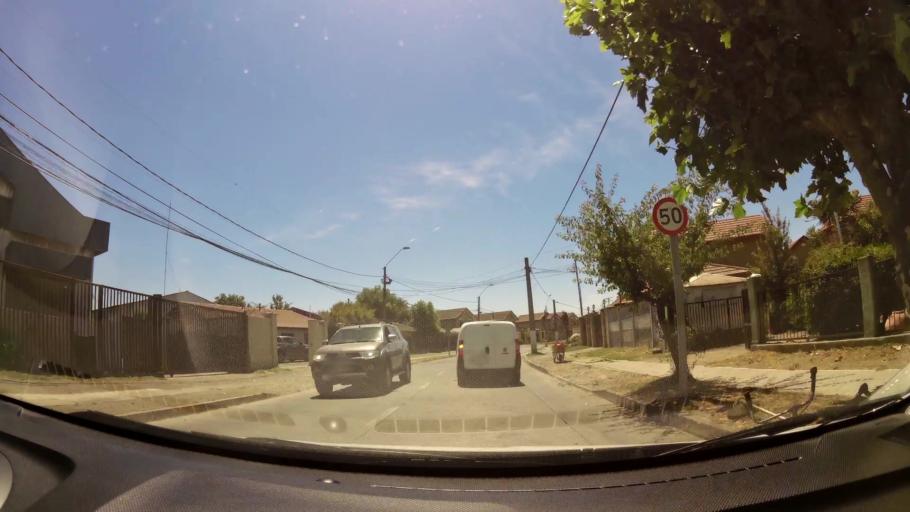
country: CL
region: Biobio
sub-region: Provincia de Concepcion
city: Talcahuano
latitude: -36.7563
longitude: -73.0871
